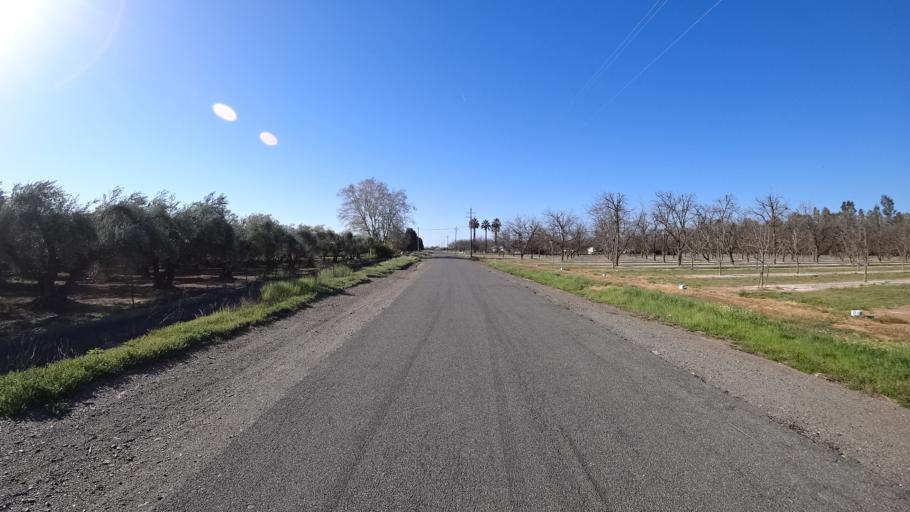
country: US
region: California
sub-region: Glenn County
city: Orland
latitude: 39.7332
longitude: -122.2392
